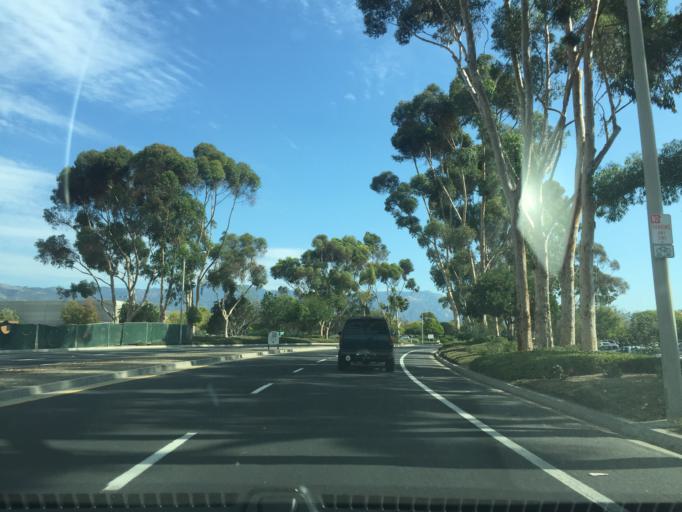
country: US
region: California
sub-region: Santa Barbara County
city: Isla Vista
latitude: 34.4323
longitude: -119.8586
